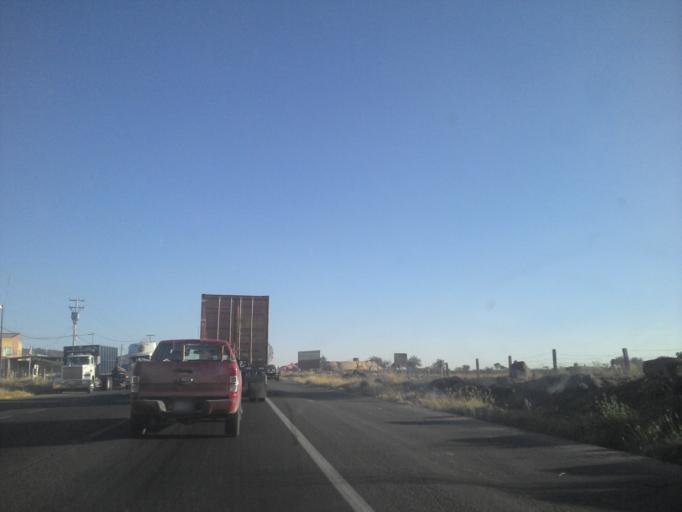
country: MX
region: Jalisco
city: Zapotlanejo
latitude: 20.6428
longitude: -103.0500
